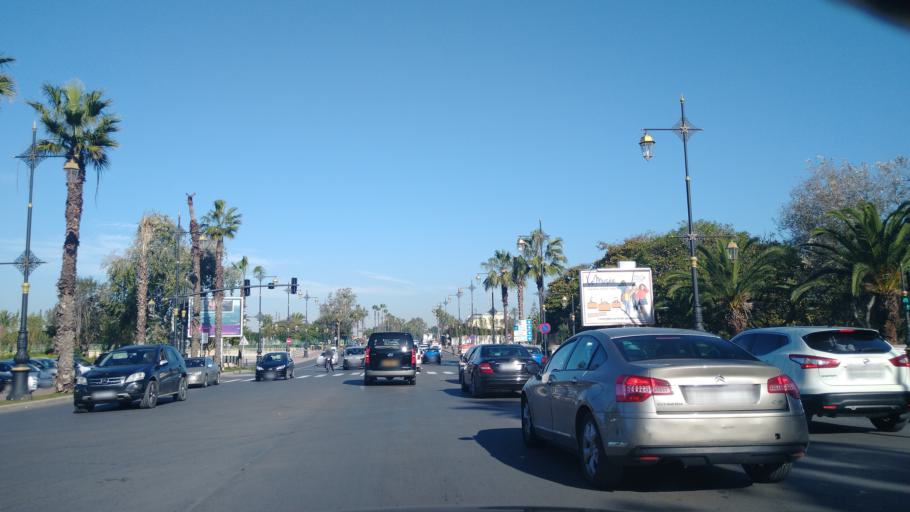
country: MA
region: Rabat-Sale-Zemmour-Zaer
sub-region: Rabat
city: Rabat
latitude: 33.9993
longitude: -6.8274
